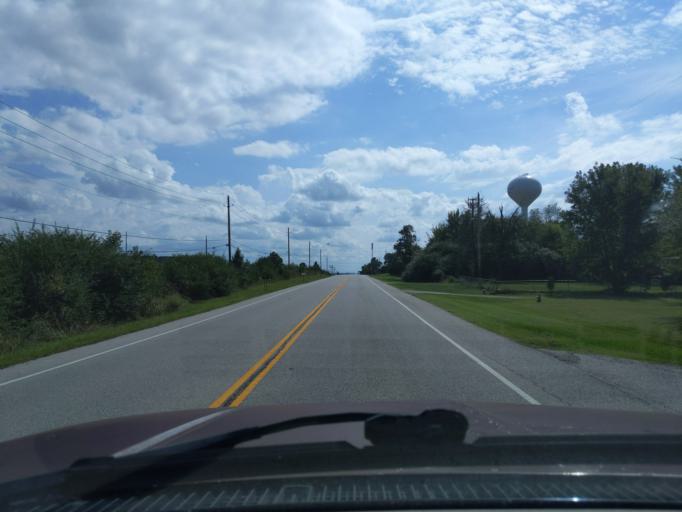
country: US
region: Oklahoma
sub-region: Tulsa County
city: Jenks
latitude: 36.0501
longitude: -96.0116
